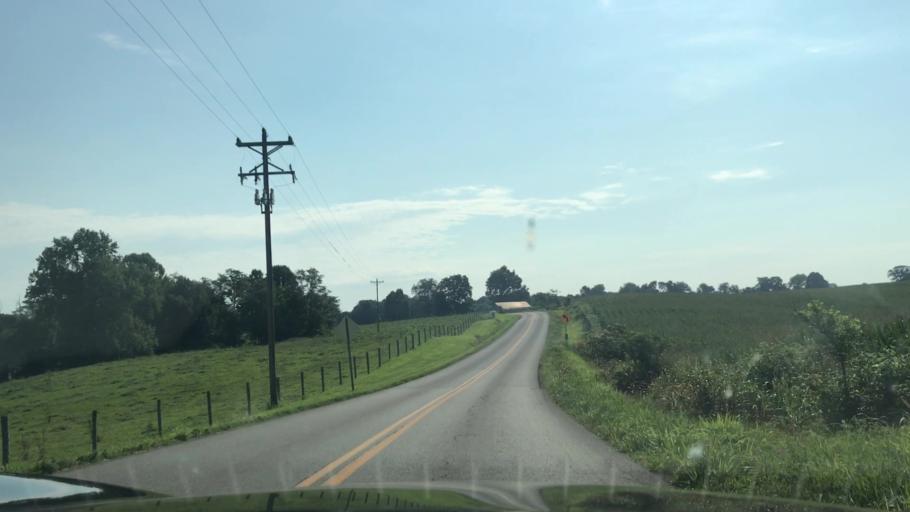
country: US
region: Kentucky
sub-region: Hart County
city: Horse Cave
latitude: 37.1872
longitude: -85.7681
